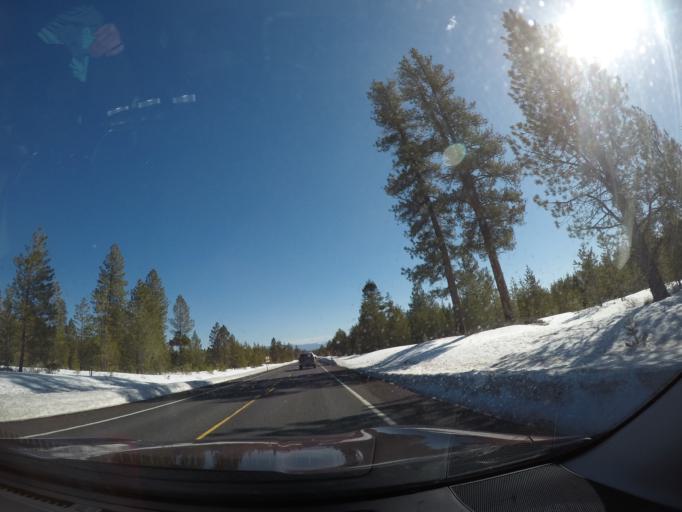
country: US
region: Oregon
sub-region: Deschutes County
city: Three Rivers
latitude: 43.8907
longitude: -121.5868
